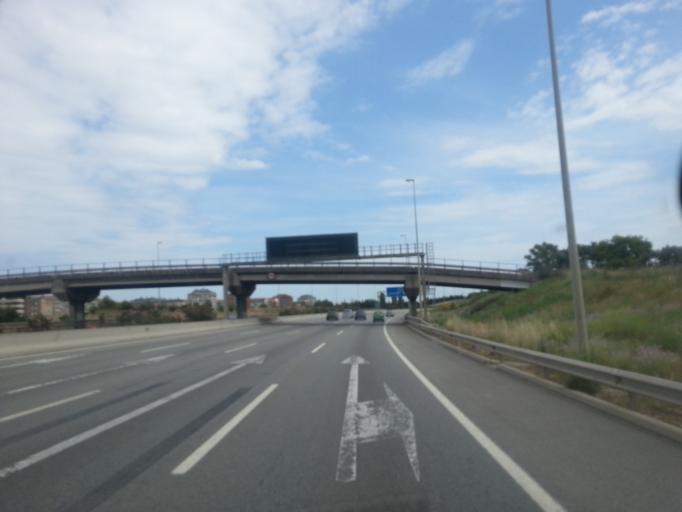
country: ES
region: Catalonia
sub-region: Provincia de Barcelona
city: Sant Feliu de Llobregat
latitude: 41.3675
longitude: 2.0467
